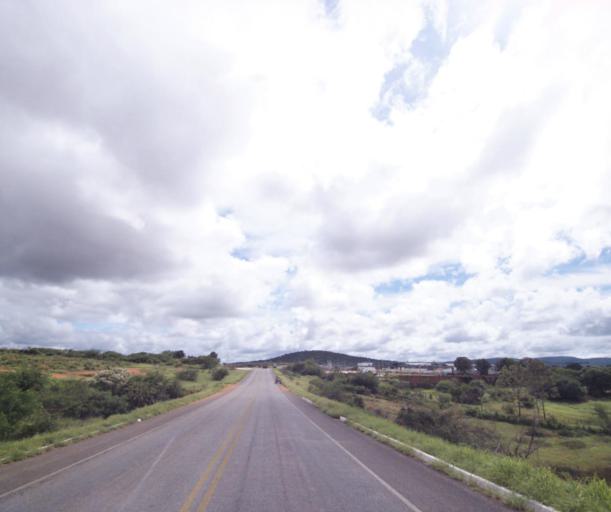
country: BR
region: Bahia
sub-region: Brumado
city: Brumado
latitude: -14.2228
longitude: -41.6706
